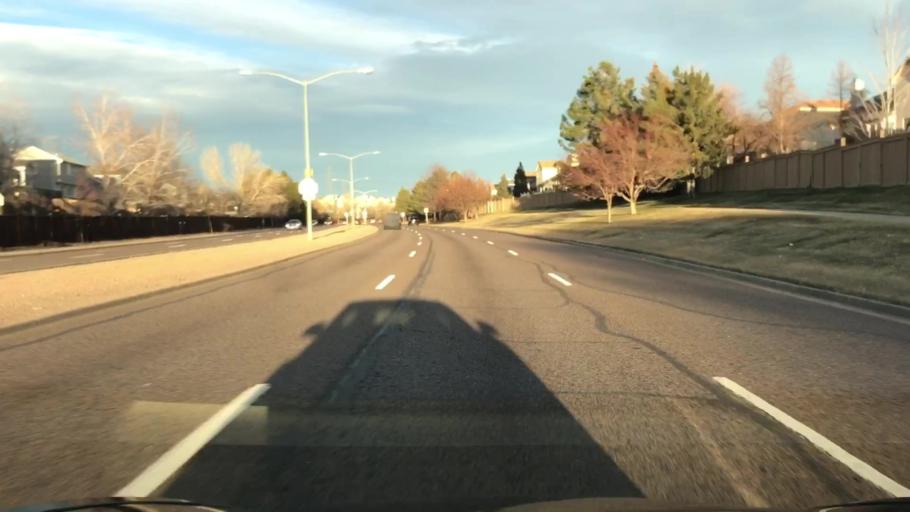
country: US
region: Colorado
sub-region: Adams County
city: Aurora
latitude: 39.6749
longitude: -104.7777
